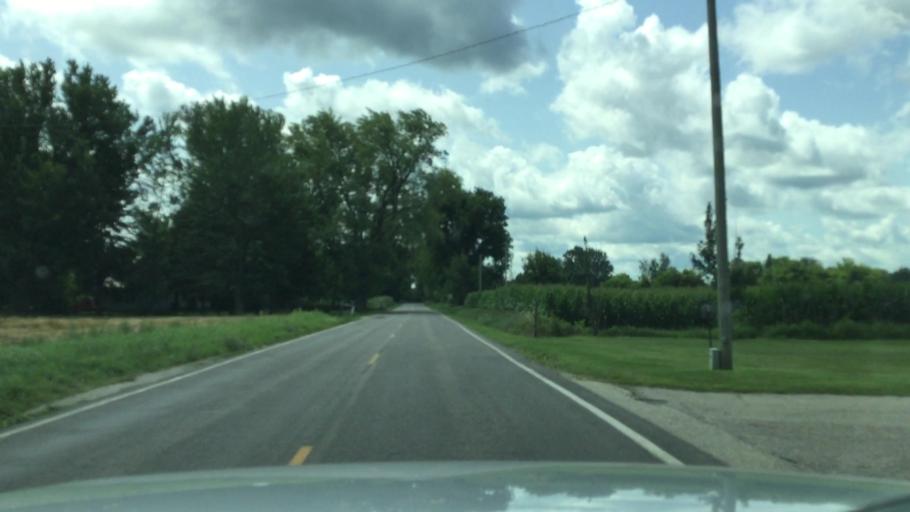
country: US
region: Michigan
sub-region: Montcalm County
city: Greenville
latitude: 43.1611
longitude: -85.2136
